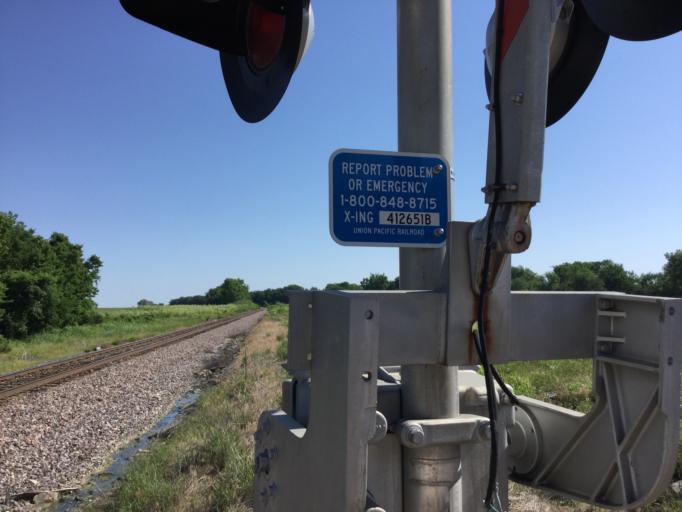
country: US
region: Kansas
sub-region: Anderson County
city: Garnett
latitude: 38.0415
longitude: -95.1668
